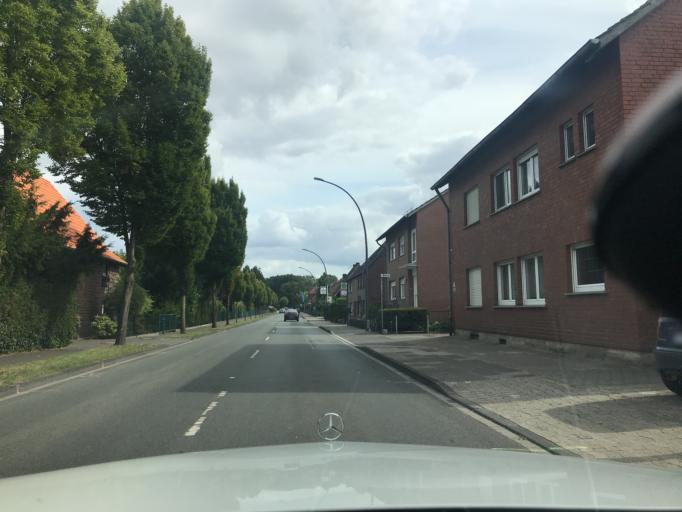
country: DE
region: North Rhine-Westphalia
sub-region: Regierungsbezirk Arnsberg
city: Welver
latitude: 51.6633
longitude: 8.0440
